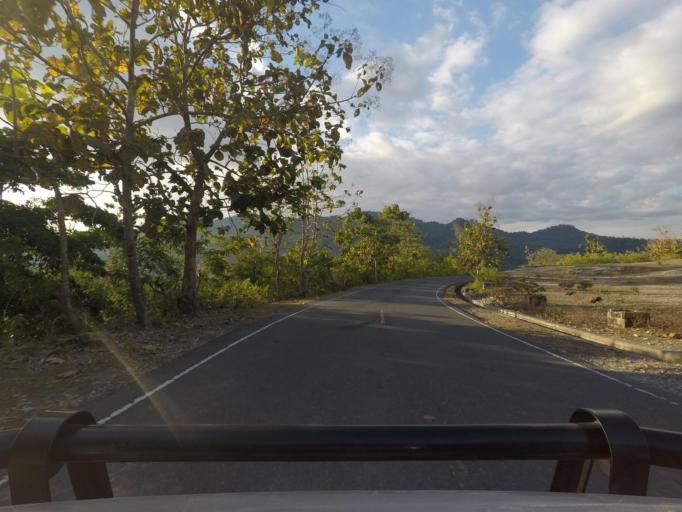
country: TL
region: Bobonaro
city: Maliana
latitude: -8.9490
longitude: 125.0934
